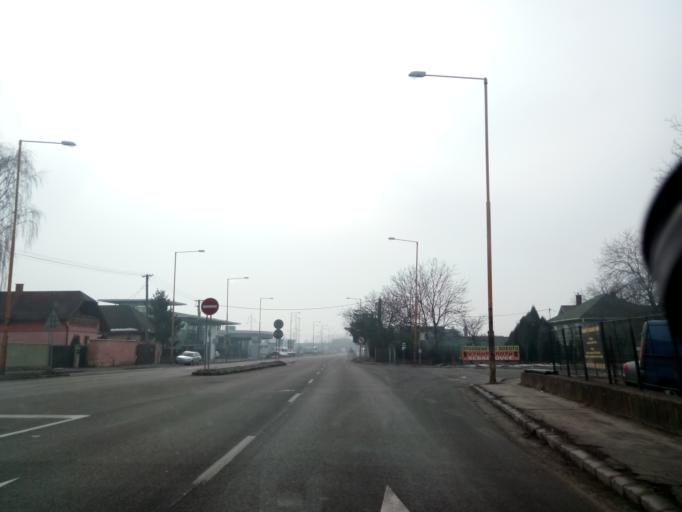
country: SK
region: Kosicky
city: Kosice
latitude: 48.6717
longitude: 21.2706
